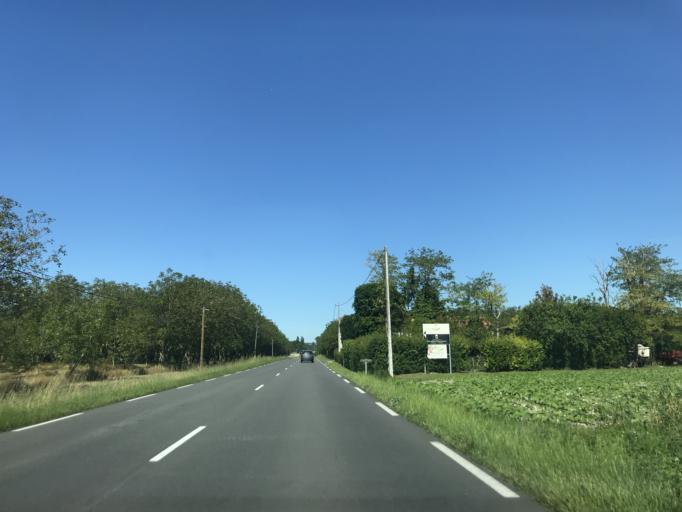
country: FR
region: Poitou-Charentes
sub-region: Departement de la Charente
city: Barbezieux-Saint-Hilaire
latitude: 45.4958
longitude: -0.2250
